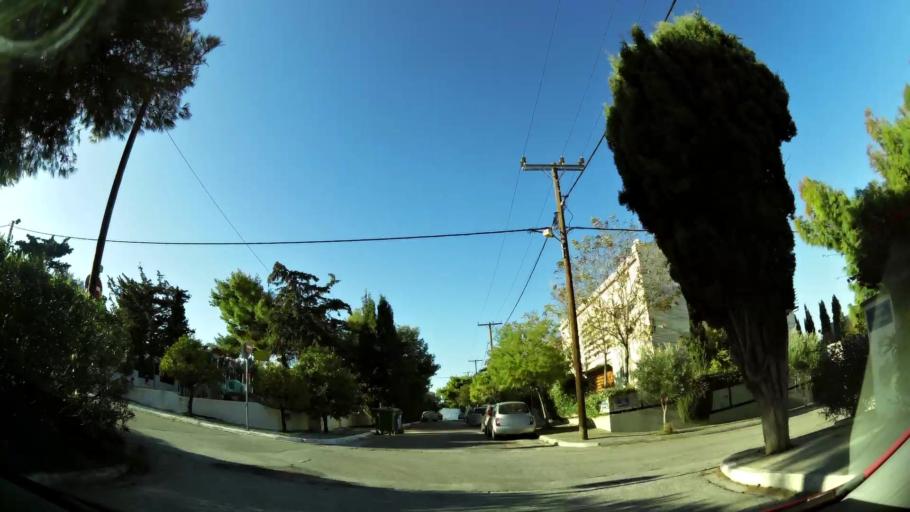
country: GR
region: Attica
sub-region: Nomarchia Anatolikis Attikis
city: Rafina
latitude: 38.0248
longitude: 24.0073
